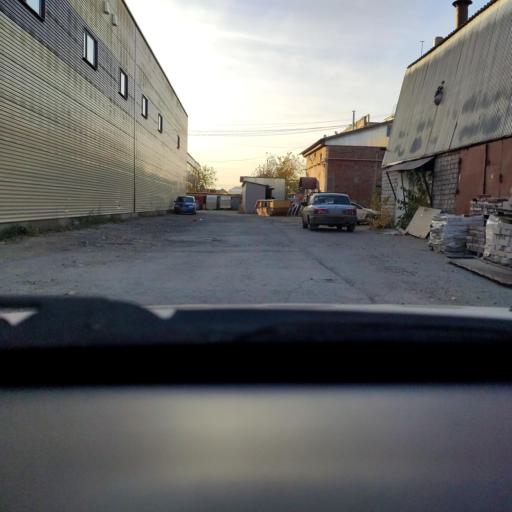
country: RU
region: Perm
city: Froly
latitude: 57.9636
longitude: 56.2746
